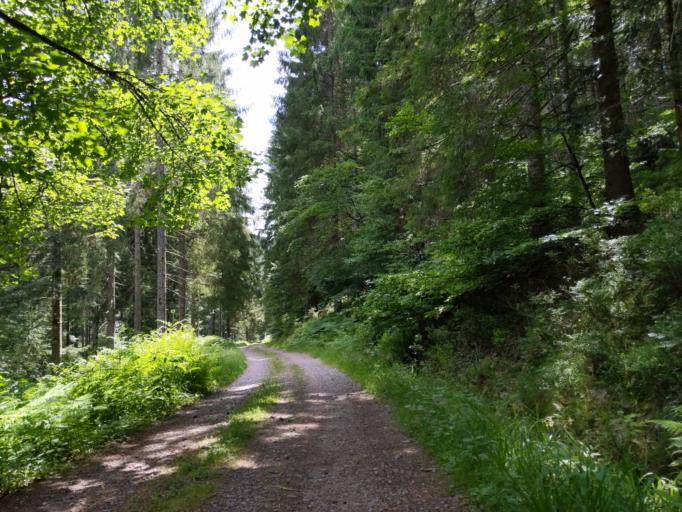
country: DE
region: Baden-Wuerttemberg
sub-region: Karlsruhe Region
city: Bad Rippoldsau-Schapbach
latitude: 48.4262
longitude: 8.3696
